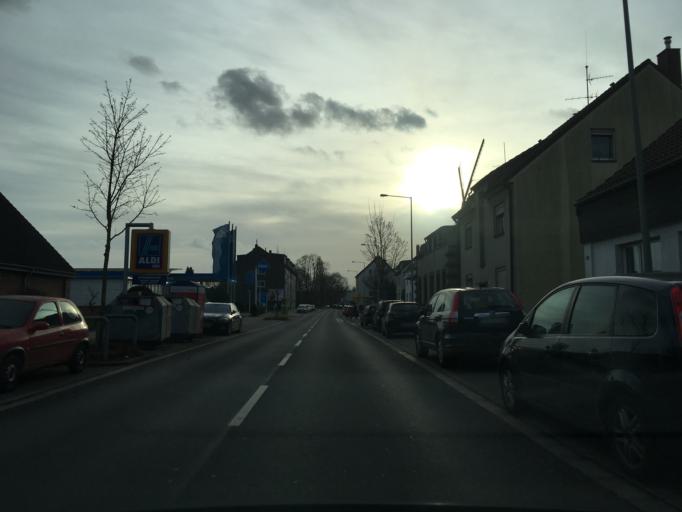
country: DE
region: North Rhine-Westphalia
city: Meiderich
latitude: 51.5221
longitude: 6.7877
